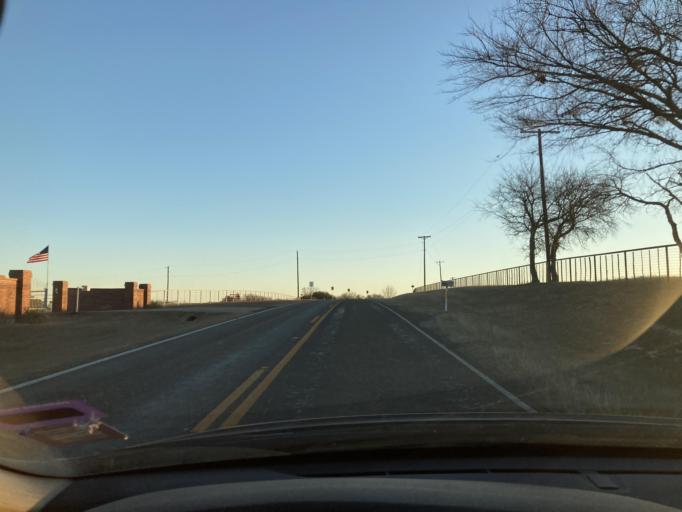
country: US
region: Texas
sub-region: Ellis County
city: Waxahachie
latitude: 32.3467
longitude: -96.8719
